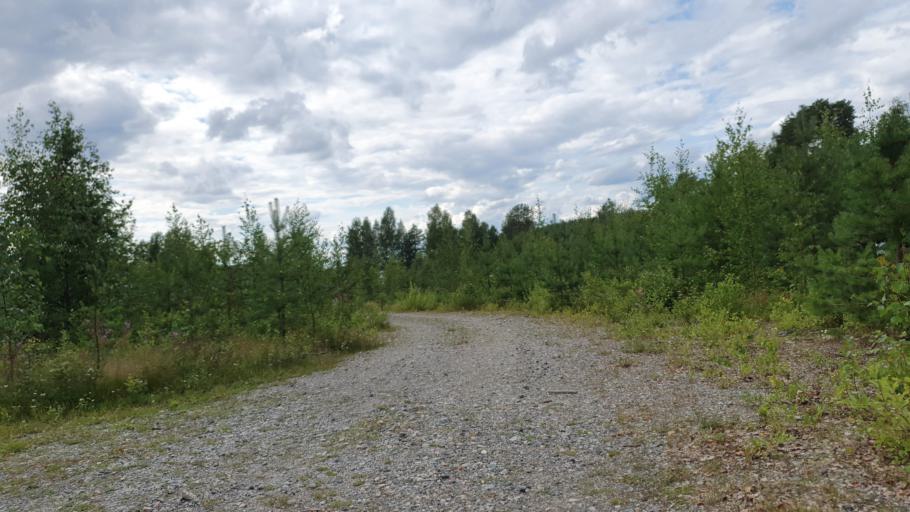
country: FI
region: Kainuu
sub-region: Kehys-Kainuu
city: Kuhmo
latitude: 64.1340
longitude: 29.5297
